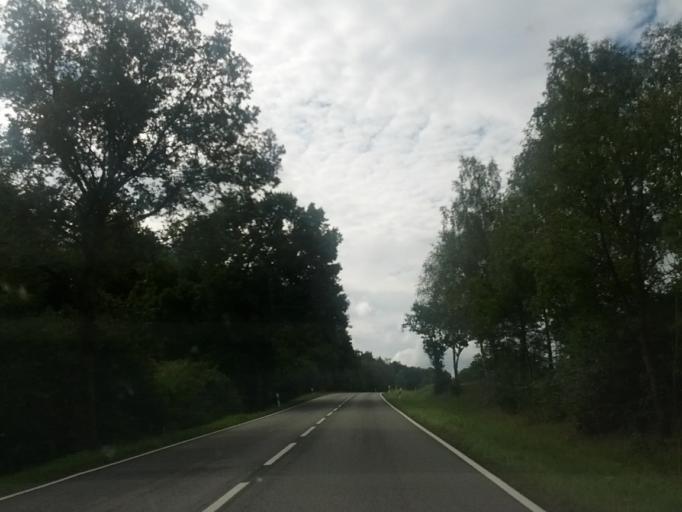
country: DE
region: Thuringia
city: Wolfsburg-Unkeroda
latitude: 50.8827
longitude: 10.2970
